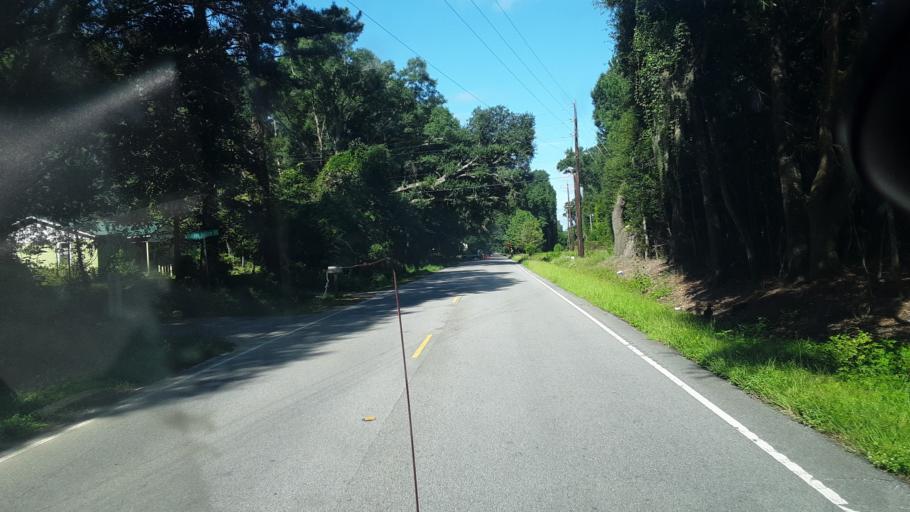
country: US
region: South Carolina
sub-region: Jasper County
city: Ridgeland
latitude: 32.5894
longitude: -80.9462
